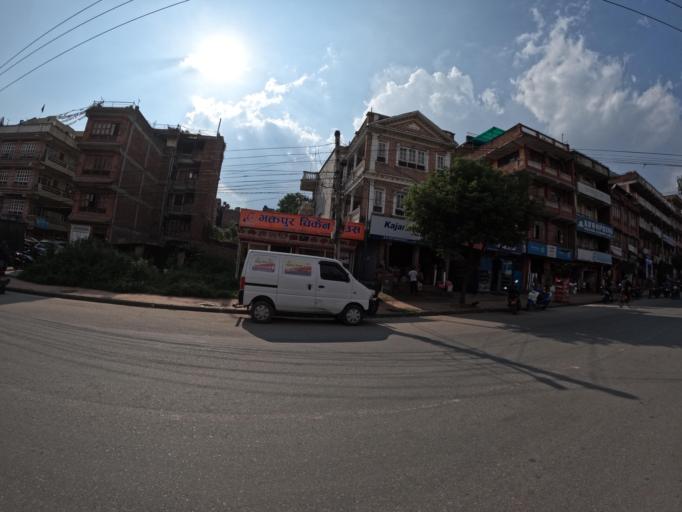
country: NP
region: Central Region
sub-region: Bagmati Zone
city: Bhaktapur
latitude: 27.6727
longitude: 85.4383
